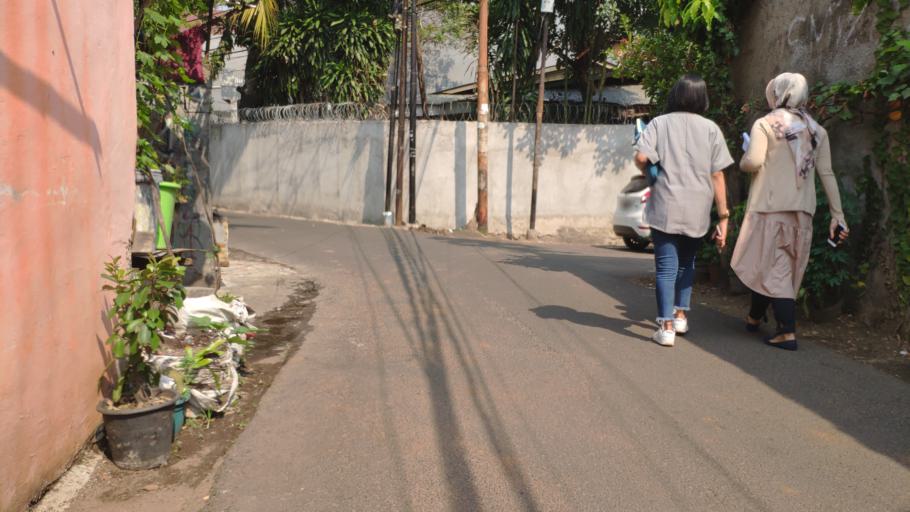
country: ID
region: Jakarta Raya
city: Jakarta
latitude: -6.2737
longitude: 106.8218
